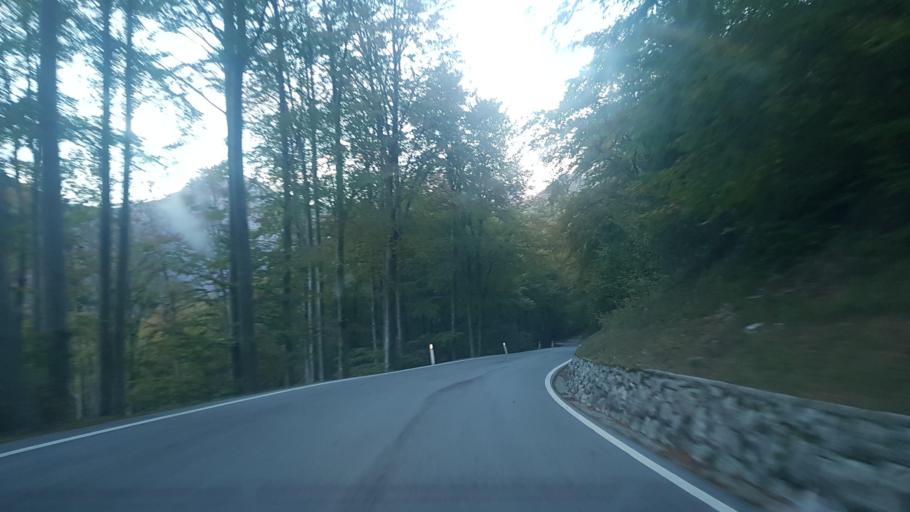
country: IT
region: Friuli Venezia Giulia
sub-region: Provincia di Udine
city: Villa Santina
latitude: 46.3519
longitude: 12.9225
